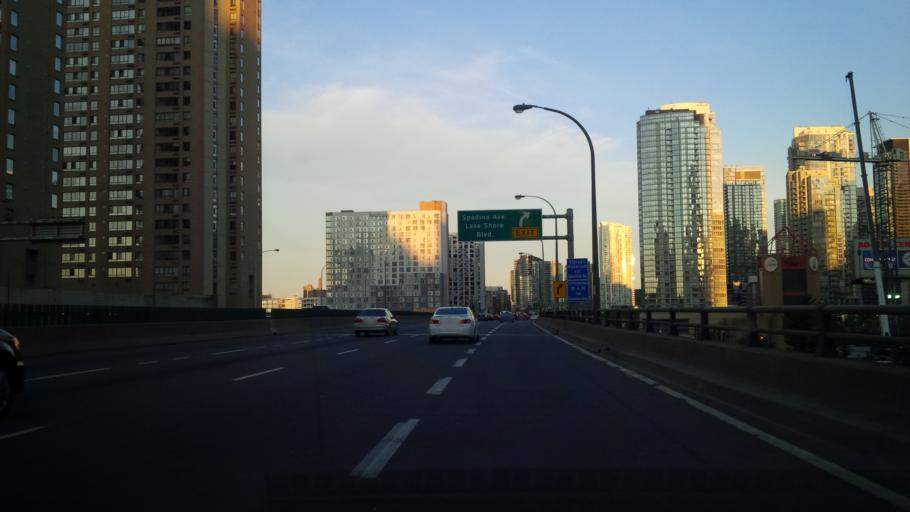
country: CA
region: Ontario
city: Toronto
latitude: 43.6402
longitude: -79.3848
